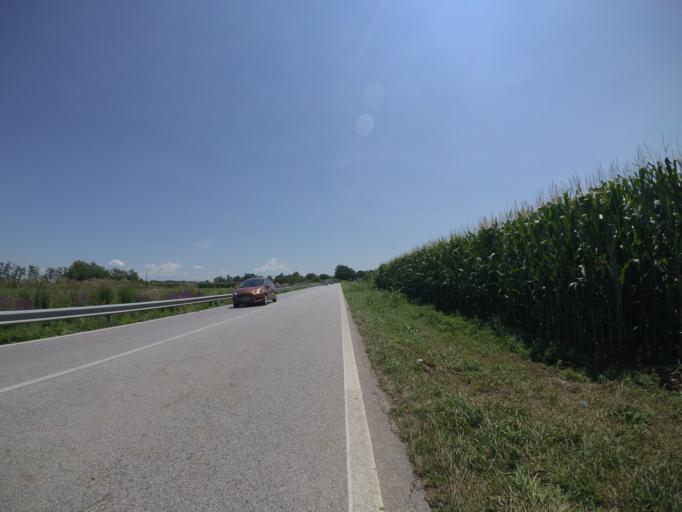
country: IT
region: Friuli Venezia Giulia
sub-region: Provincia di Udine
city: Lestizza
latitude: 45.9920
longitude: 13.1292
